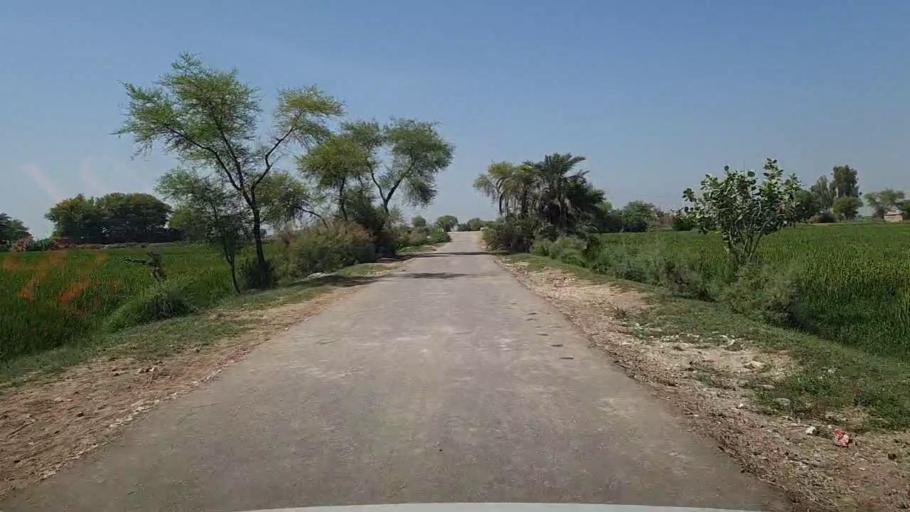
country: PK
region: Sindh
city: Kandhkot
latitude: 28.3225
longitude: 69.3382
